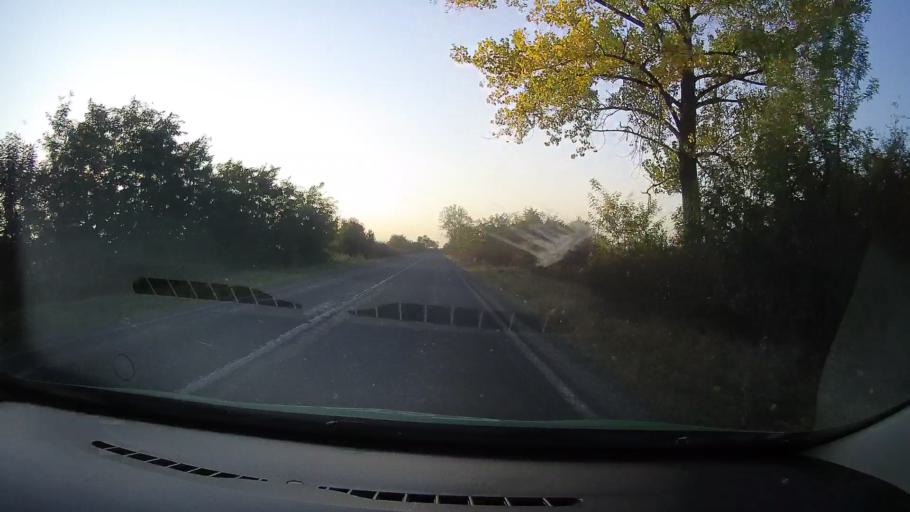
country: RO
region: Arad
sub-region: Comuna Bocsig
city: Bocsig
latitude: 46.4253
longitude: 21.9135
